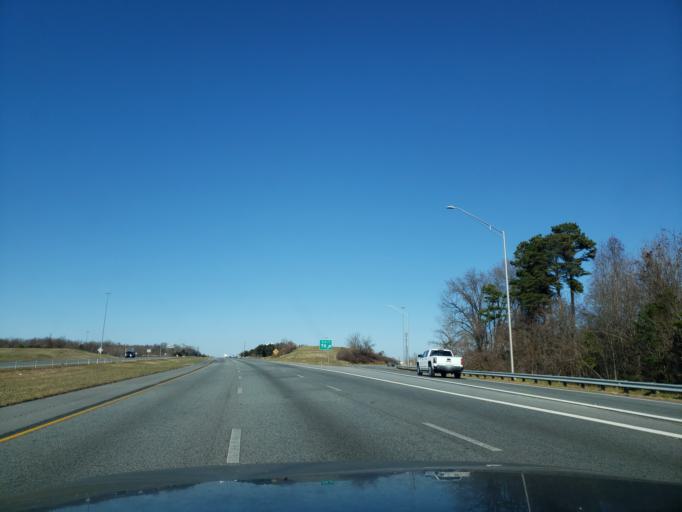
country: US
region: North Carolina
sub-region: Guilford County
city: High Point
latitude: 35.9621
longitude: -79.9745
